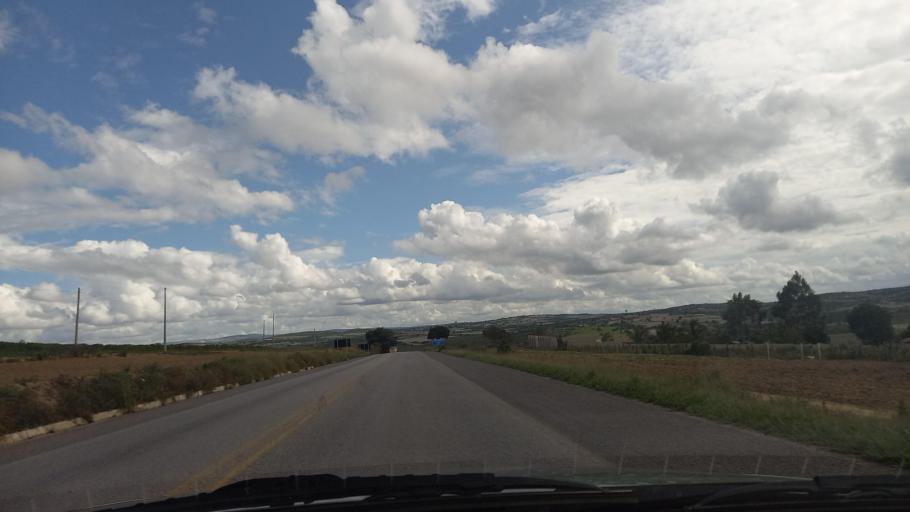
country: BR
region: Pernambuco
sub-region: Lajedo
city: Lajedo
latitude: -8.7227
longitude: -36.4275
